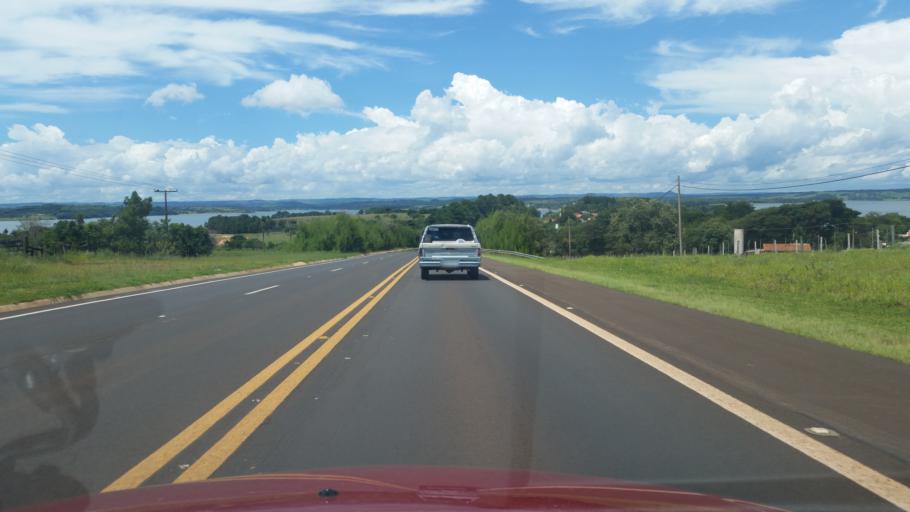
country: BR
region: Sao Paulo
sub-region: Itai
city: Itai
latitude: -23.2818
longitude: -49.0274
